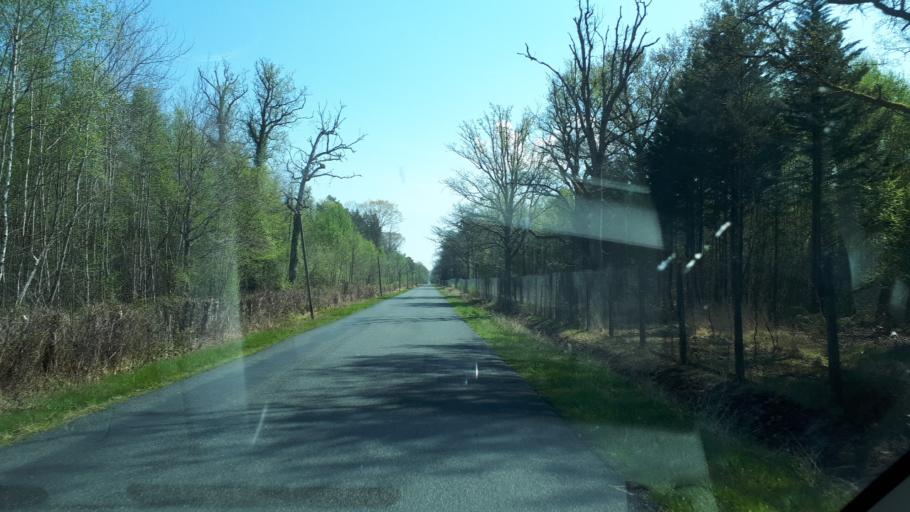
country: FR
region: Centre
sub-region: Departement du Cher
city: Neuvy-sur-Barangeon
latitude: 47.3180
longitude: 2.2228
